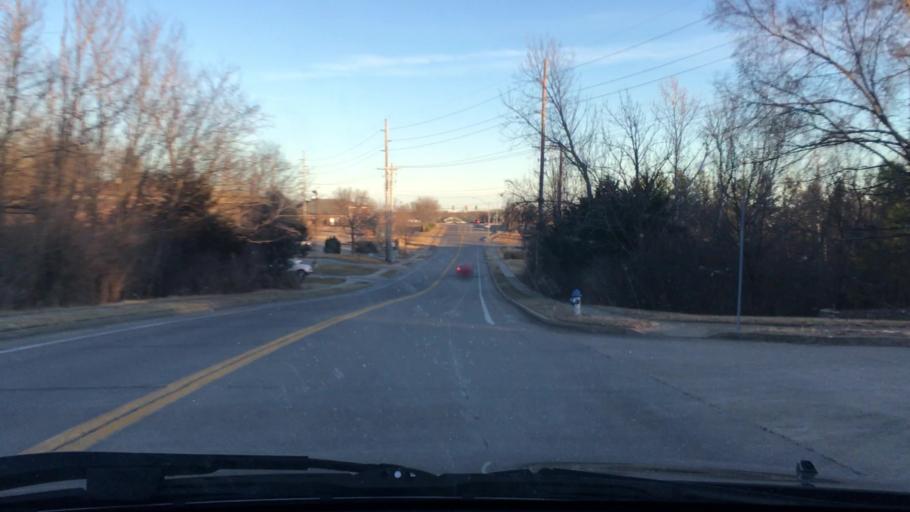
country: US
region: Missouri
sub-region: Boone County
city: Columbia
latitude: 38.9315
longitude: -92.3664
